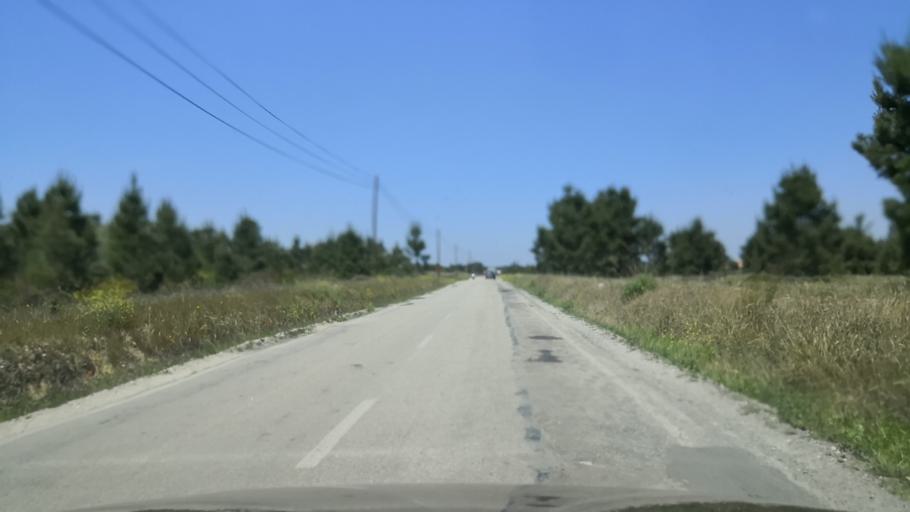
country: PT
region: Setubal
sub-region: Palmela
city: Palmela
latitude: 38.6251
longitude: -8.7466
